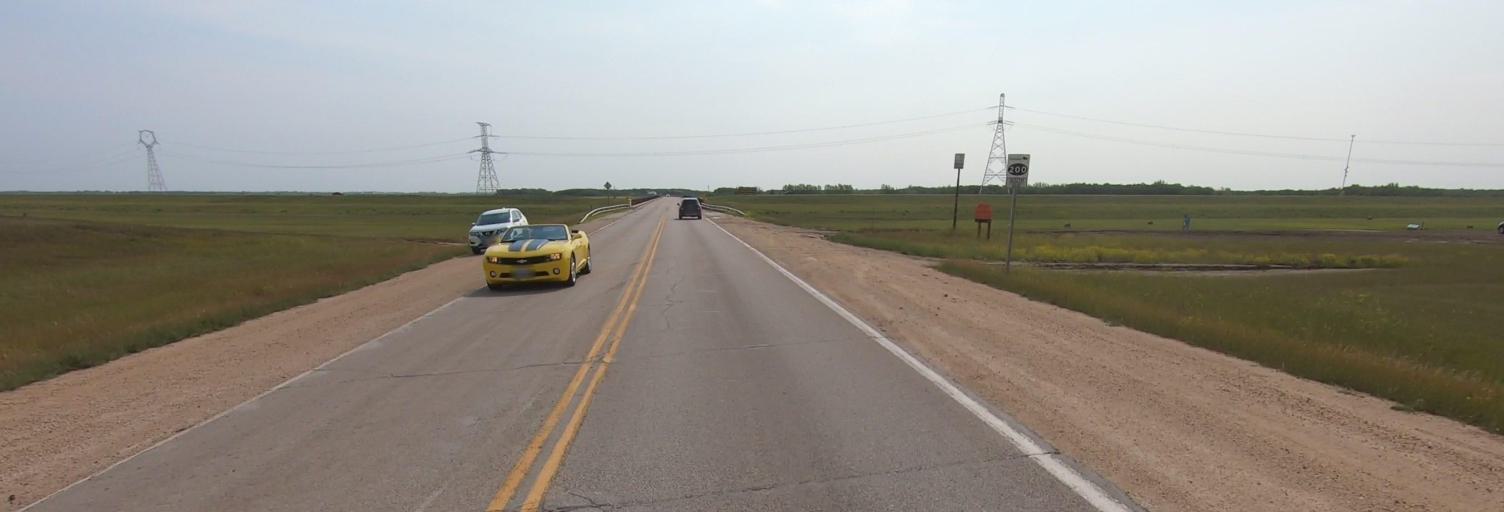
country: CA
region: Manitoba
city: Winnipeg
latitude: 49.7575
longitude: -97.1242
